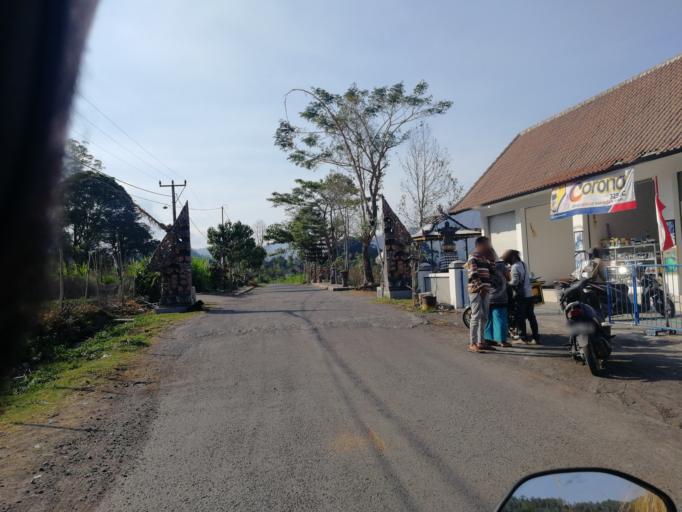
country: ID
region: Bali
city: Banjar Buahan
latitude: -8.2852
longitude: 115.3889
